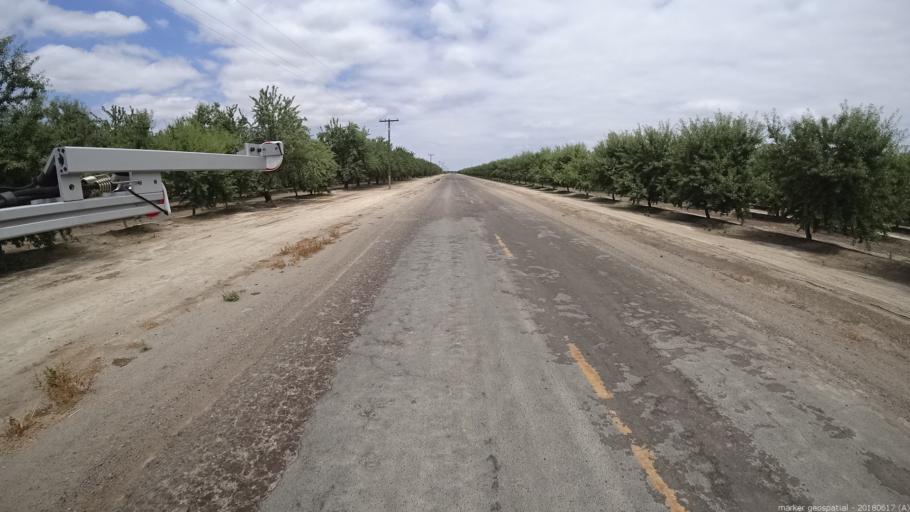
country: US
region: California
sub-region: Fresno County
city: Kerman
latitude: 36.8298
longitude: -120.1871
